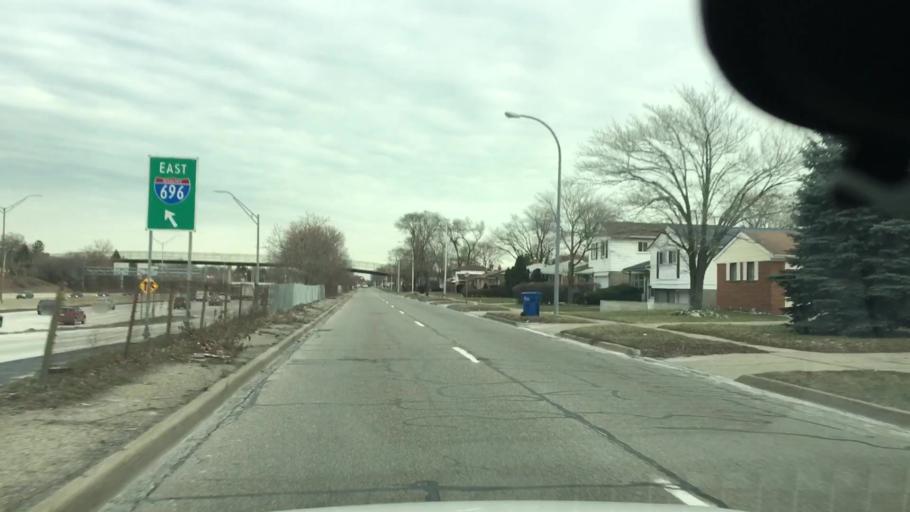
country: US
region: Michigan
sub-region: Oakland County
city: Madison Heights
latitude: 42.4906
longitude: -83.0745
